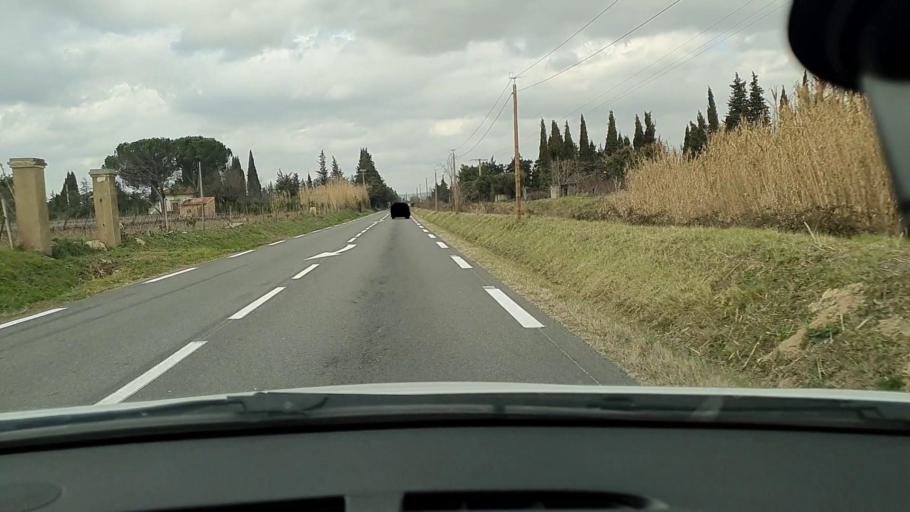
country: FR
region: Languedoc-Roussillon
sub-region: Departement du Gard
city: Montfrin
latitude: 43.8716
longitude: 4.5833
